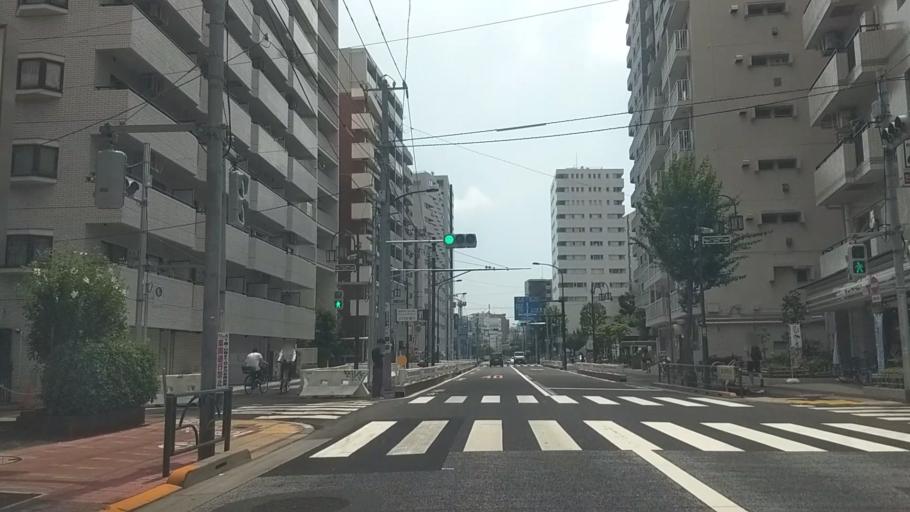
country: JP
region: Tokyo
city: Tokyo
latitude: 35.6167
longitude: 139.7070
